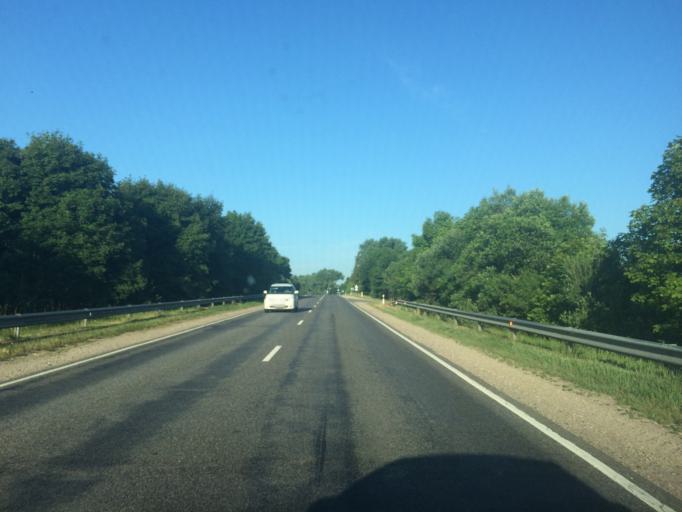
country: LT
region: Utenos apskritis
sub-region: Anyksciai
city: Anyksciai
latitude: 55.3797
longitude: 25.0332
